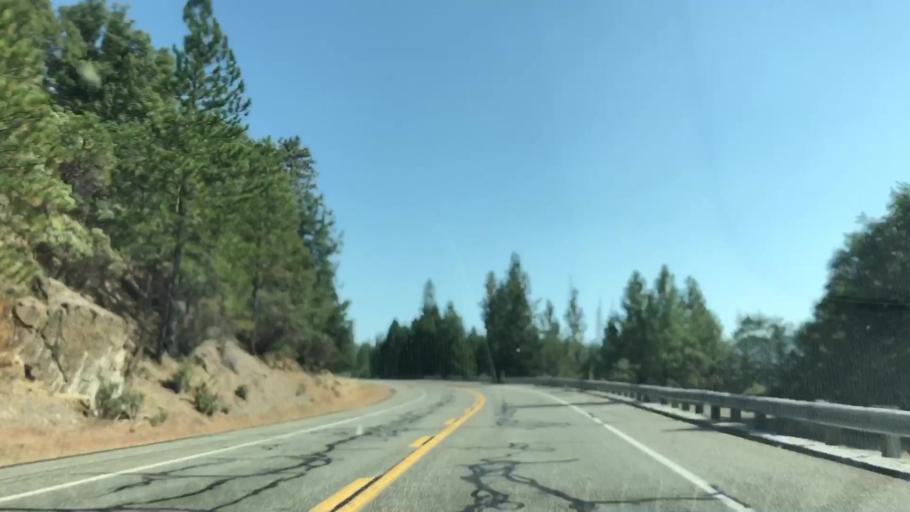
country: US
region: California
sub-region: Tuolumne County
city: Tuolumne City
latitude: 37.8348
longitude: -120.2034
